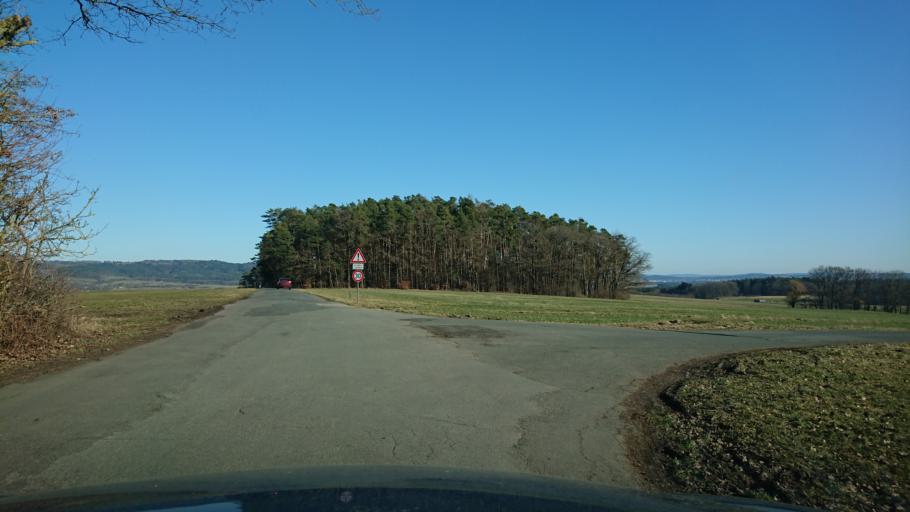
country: DE
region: Bavaria
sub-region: Upper Franconia
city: Langensendelbach
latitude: 49.6264
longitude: 11.0894
